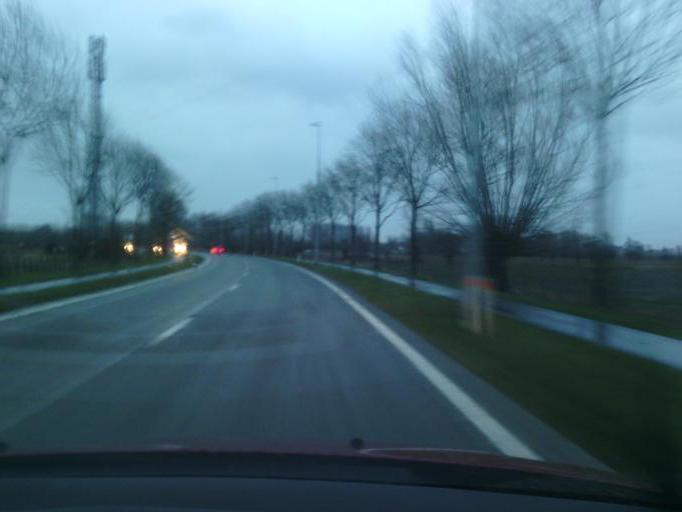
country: BE
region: Flanders
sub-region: Provincie Oost-Vlaanderen
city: Lokeren
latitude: 51.0947
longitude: 3.9765
